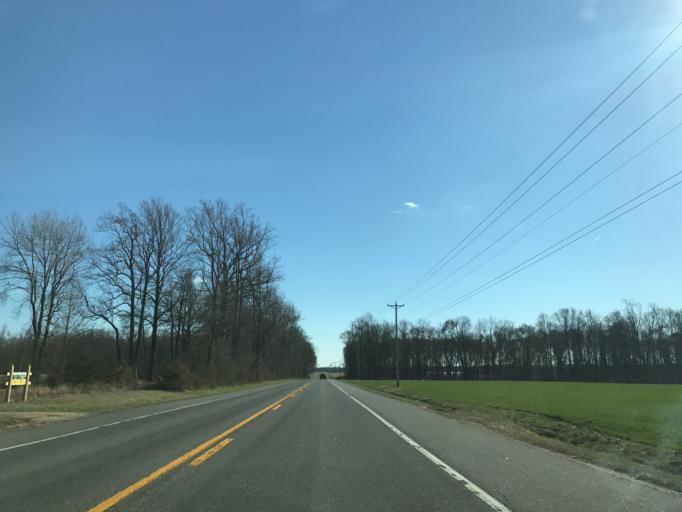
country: US
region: Maryland
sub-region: Queen Anne's County
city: Kingstown
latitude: 39.1722
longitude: -75.8595
